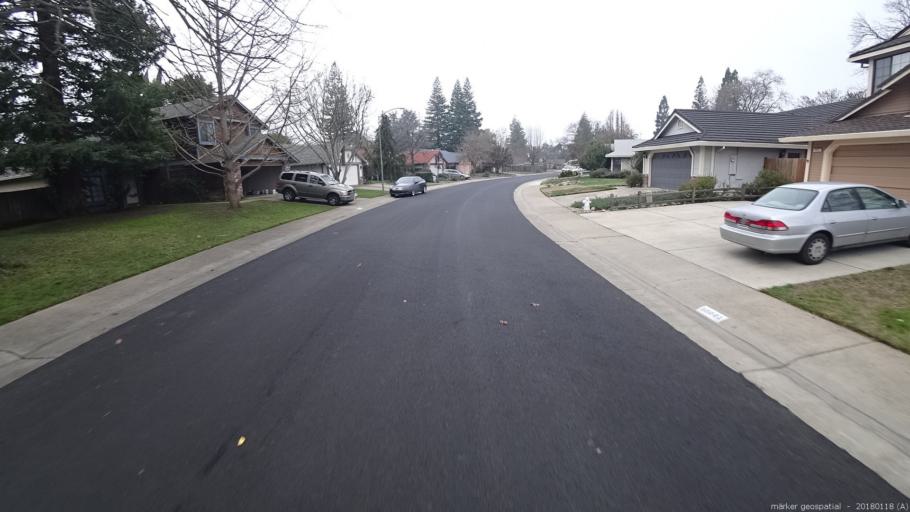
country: US
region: California
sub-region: Sacramento County
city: Rancho Cordova
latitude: 38.5871
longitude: -121.3217
